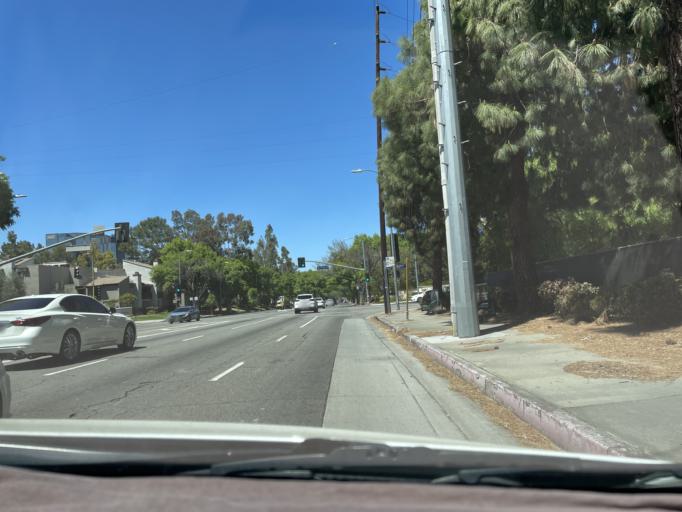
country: US
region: California
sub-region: Los Angeles County
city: Woodland Hills
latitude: 34.1727
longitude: -118.5974
